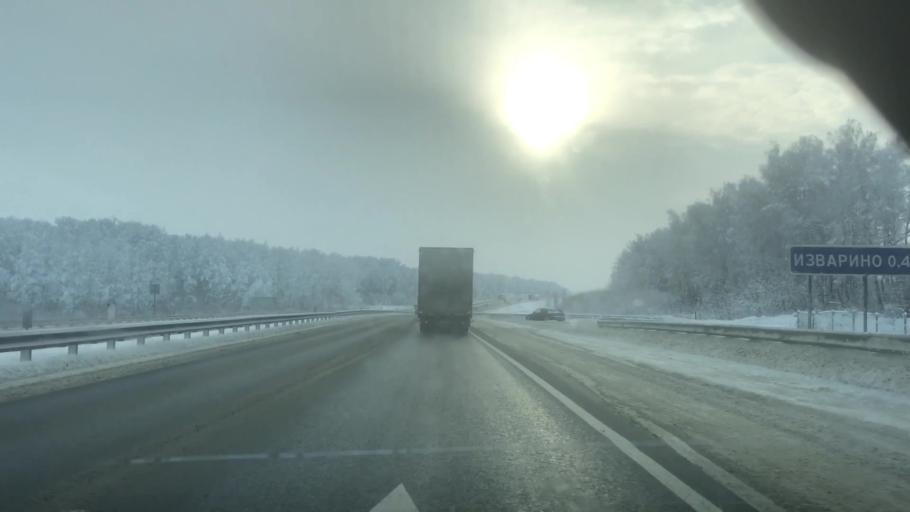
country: RU
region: Tula
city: Venev
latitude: 54.5173
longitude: 38.1701
